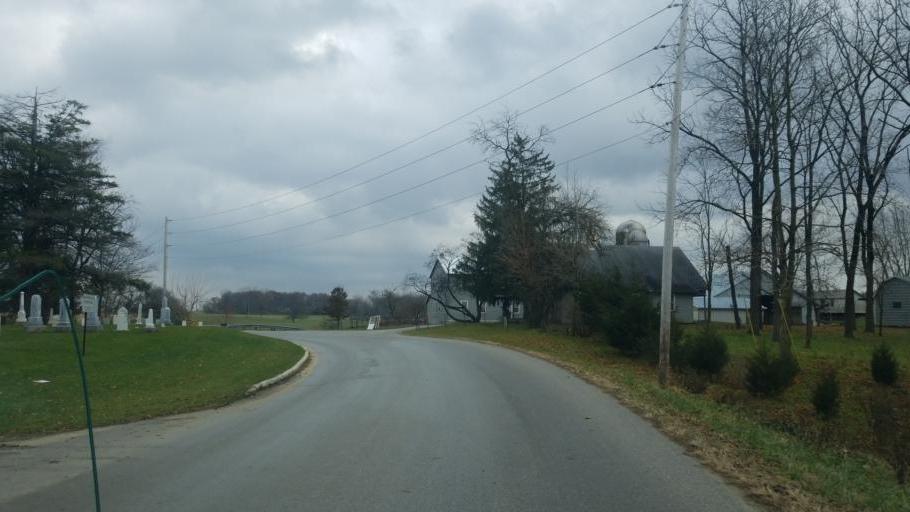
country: US
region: Indiana
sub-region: Jay County
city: Portland
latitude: 40.5115
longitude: -84.9728
